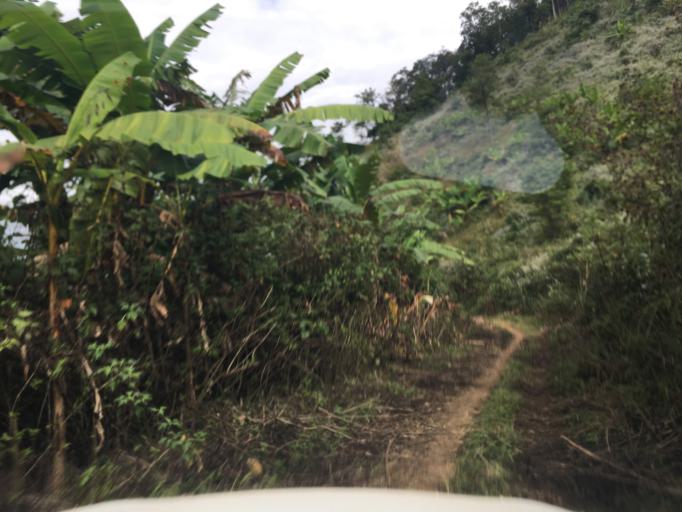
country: LA
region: Houaphan
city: Viengthong
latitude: 19.9143
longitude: 103.2997
